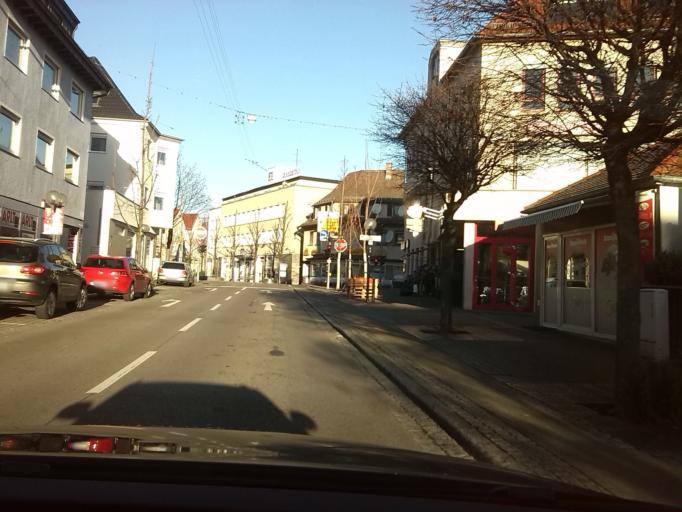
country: DE
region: Baden-Wuerttemberg
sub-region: Regierungsbezirk Stuttgart
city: Fellbach
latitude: 48.8140
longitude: 9.2753
